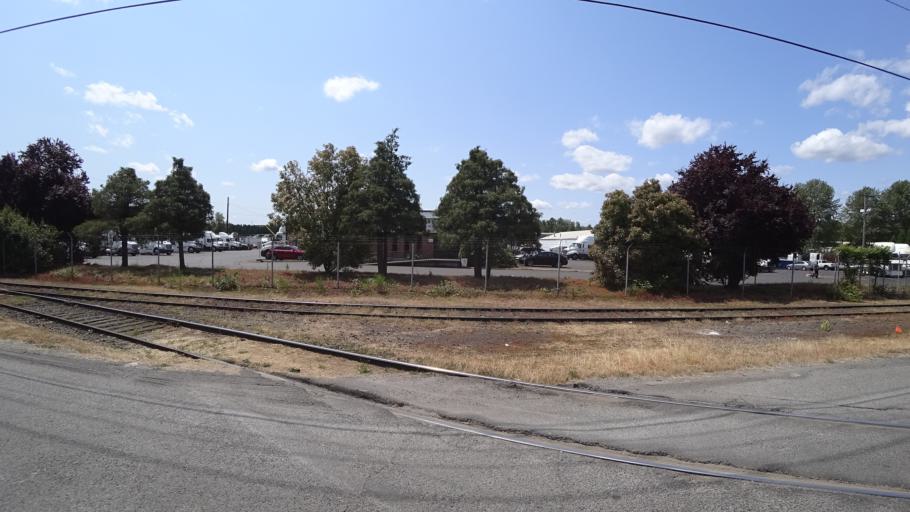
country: US
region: Washington
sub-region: Clark County
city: Vancouver
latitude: 45.6150
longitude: -122.7120
